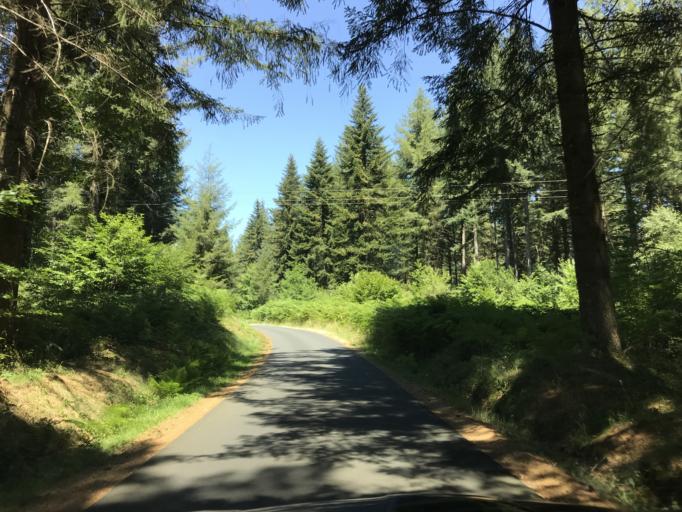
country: FR
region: Limousin
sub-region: Departement de la Correze
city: Neuvic
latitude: 45.3794
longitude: 2.2316
